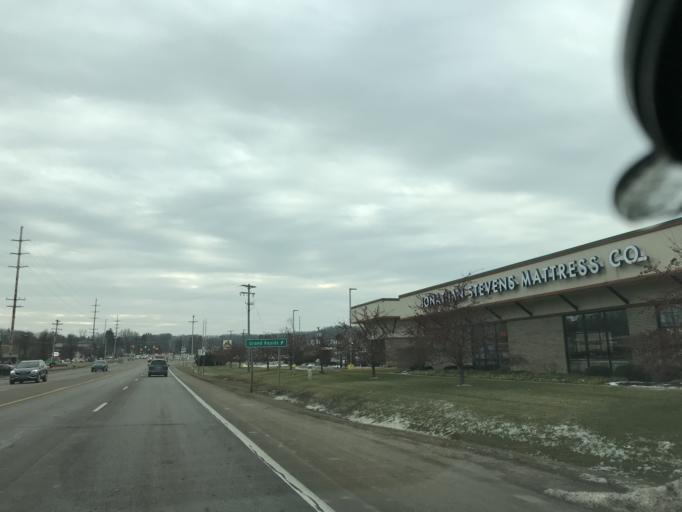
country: US
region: Michigan
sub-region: Kent County
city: Northview
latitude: 43.0583
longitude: -85.5799
